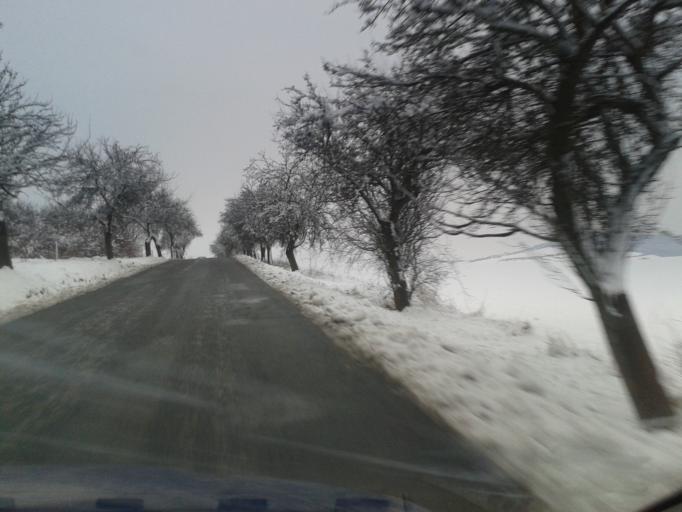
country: CZ
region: Central Bohemia
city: Revnice
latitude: 49.9214
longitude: 14.1647
